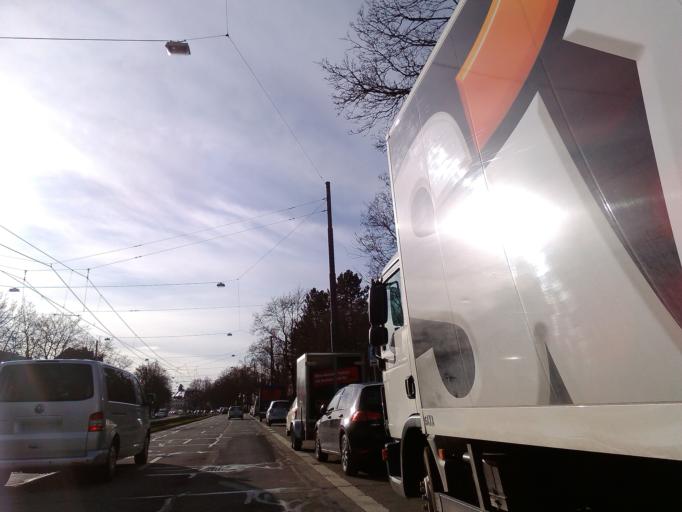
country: DE
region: Bavaria
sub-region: Upper Bavaria
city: Munich
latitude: 48.0995
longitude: 11.5656
